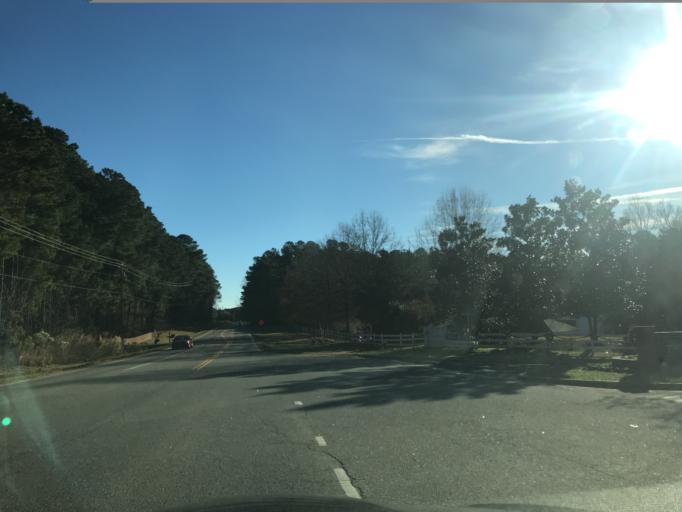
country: US
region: North Carolina
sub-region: Wake County
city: West Raleigh
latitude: 35.9063
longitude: -78.7011
